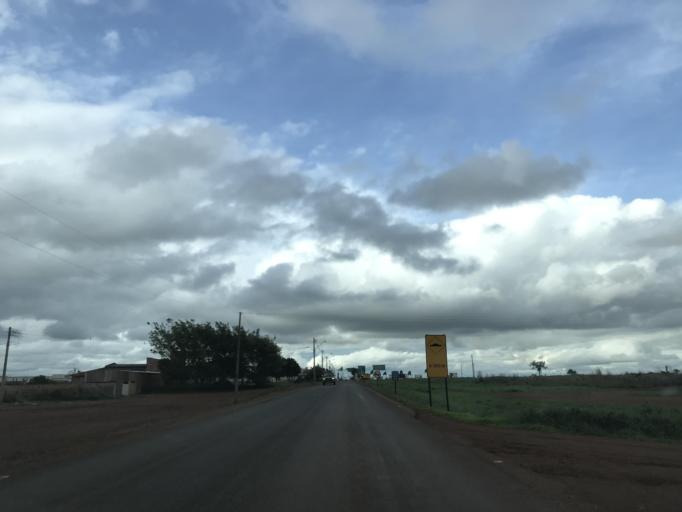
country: BR
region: Goias
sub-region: Vianopolis
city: Vianopolis
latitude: -16.7667
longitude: -48.5222
